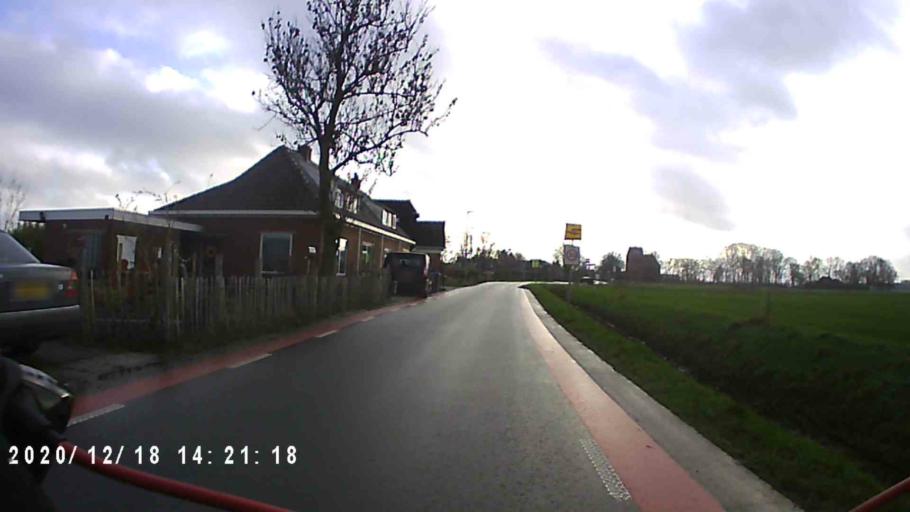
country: NL
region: Groningen
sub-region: Gemeente Bedum
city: Bedum
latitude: 53.2514
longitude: 6.6474
